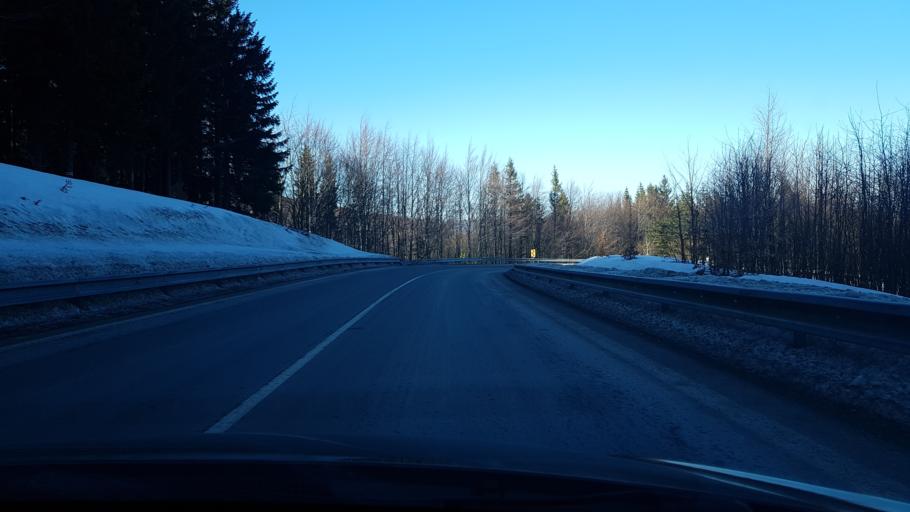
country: CZ
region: Olomoucky
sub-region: Okres Jesenik
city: Jesenik
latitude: 50.1431
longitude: 17.1618
